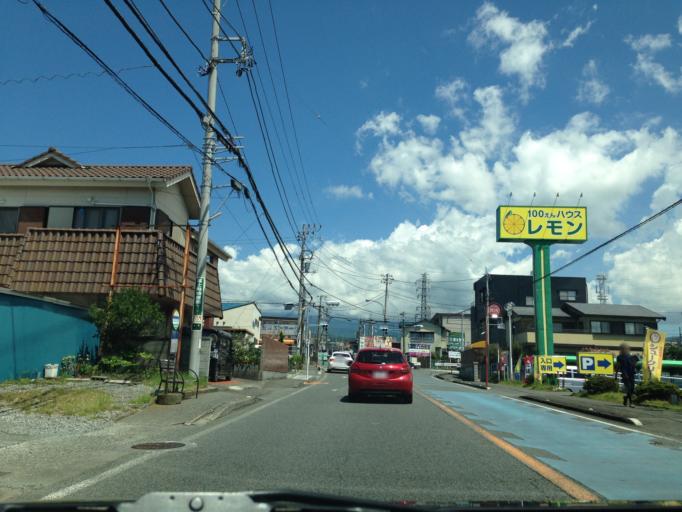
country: JP
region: Shizuoka
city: Fuji
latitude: 35.1725
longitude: 138.6901
